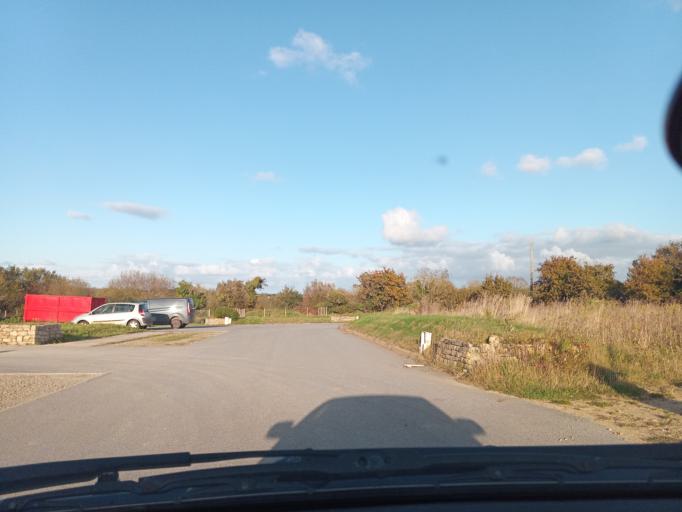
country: FR
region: Brittany
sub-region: Departement du Finistere
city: Esquibien
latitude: 48.0340
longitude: -4.5636
